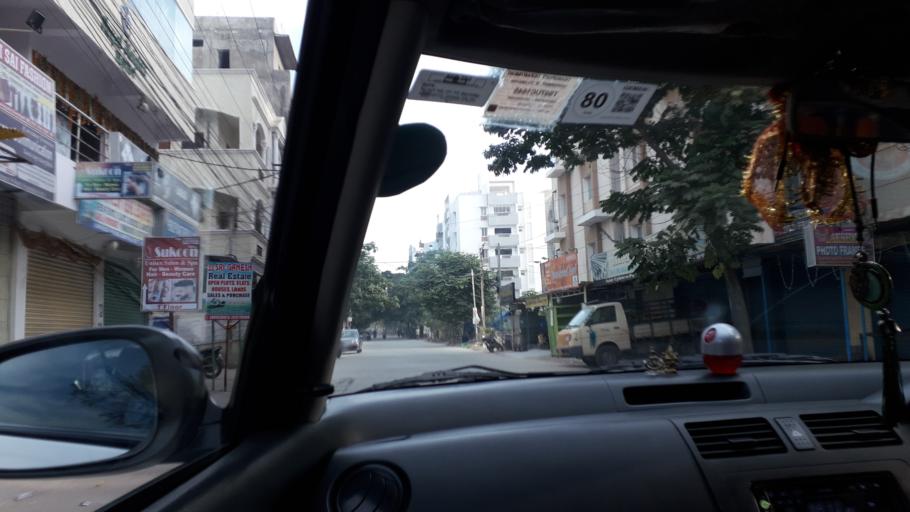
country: IN
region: Telangana
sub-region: Hyderabad
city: Hyderabad
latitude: 17.3939
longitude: 78.3768
